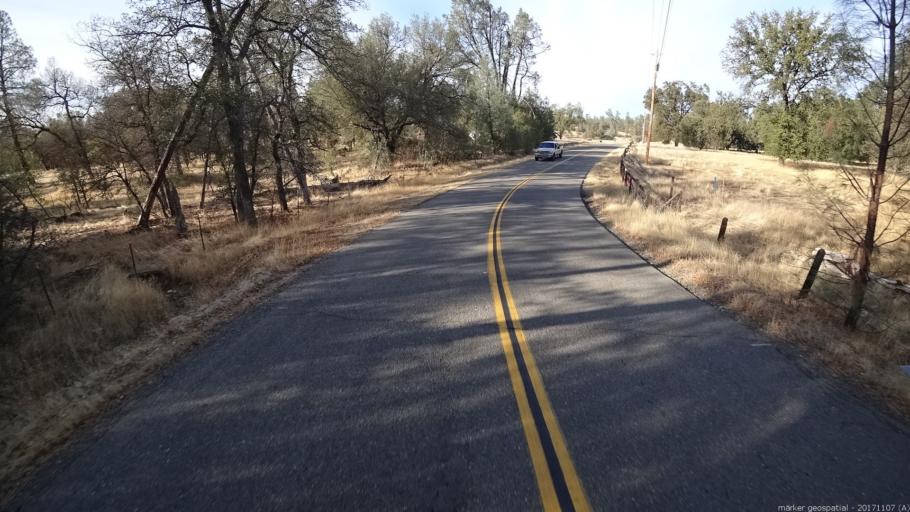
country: US
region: California
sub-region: Shasta County
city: Redding
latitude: 40.5057
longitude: -122.4471
